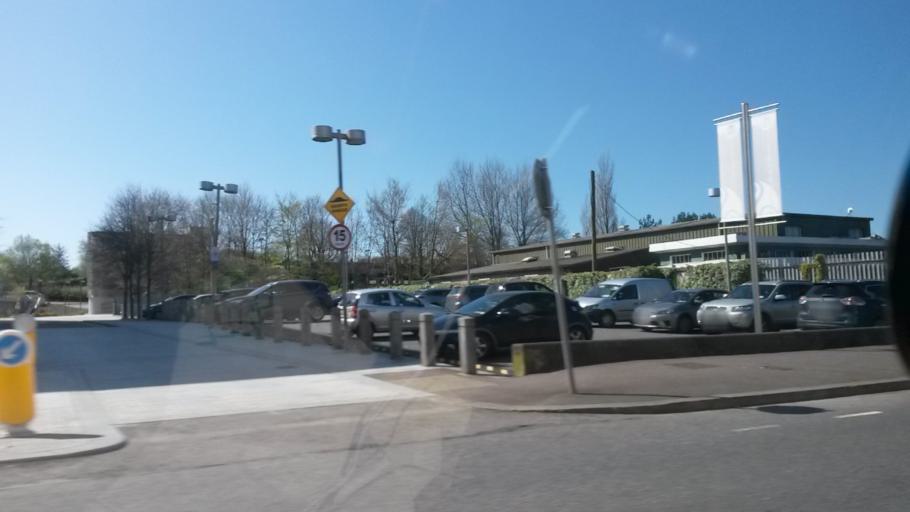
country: IE
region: Munster
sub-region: County Cork
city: Cork
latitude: 51.8932
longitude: -8.5095
